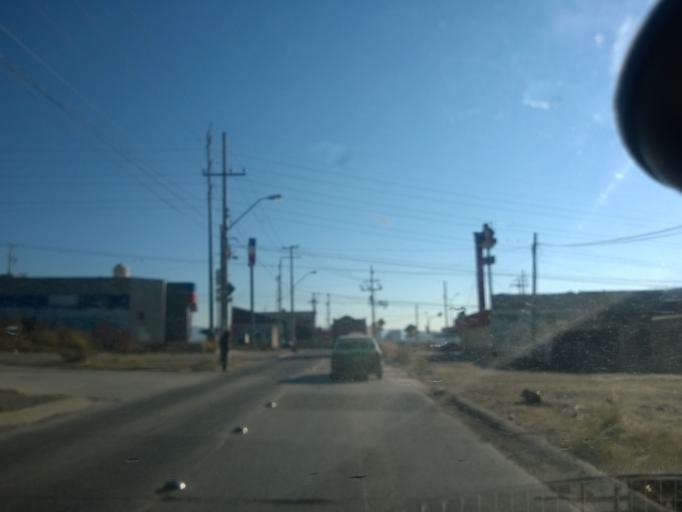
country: MX
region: Guanajuato
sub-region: Leon
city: La Ermita
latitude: 21.1519
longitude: -101.7304
